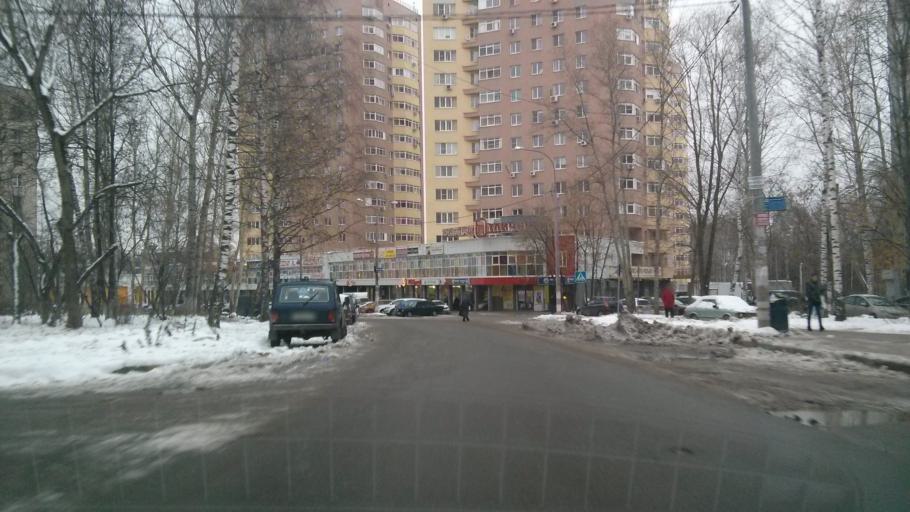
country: RU
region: Nizjnij Novgorod
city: Nizhniy Novgorod
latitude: 56.2931
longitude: 44.0441
